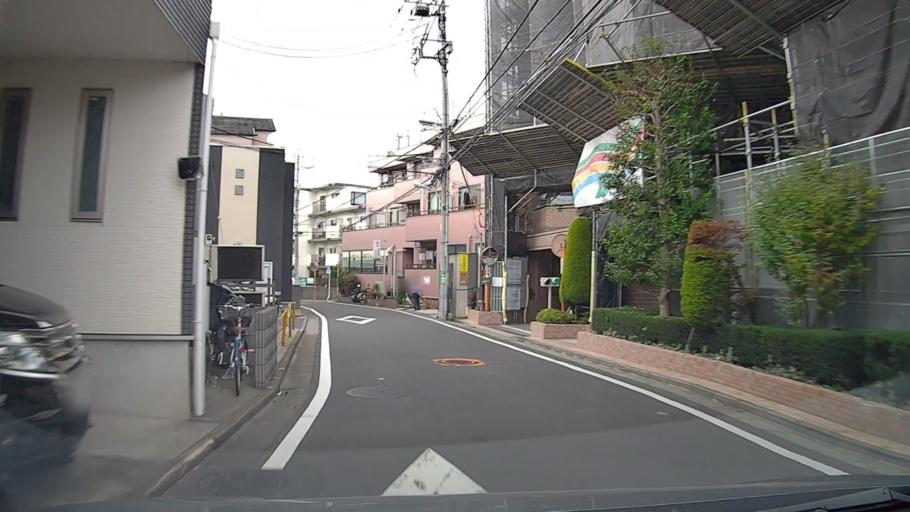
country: JP
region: Saitama
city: Wako
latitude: 35.7337
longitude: 139.6105
